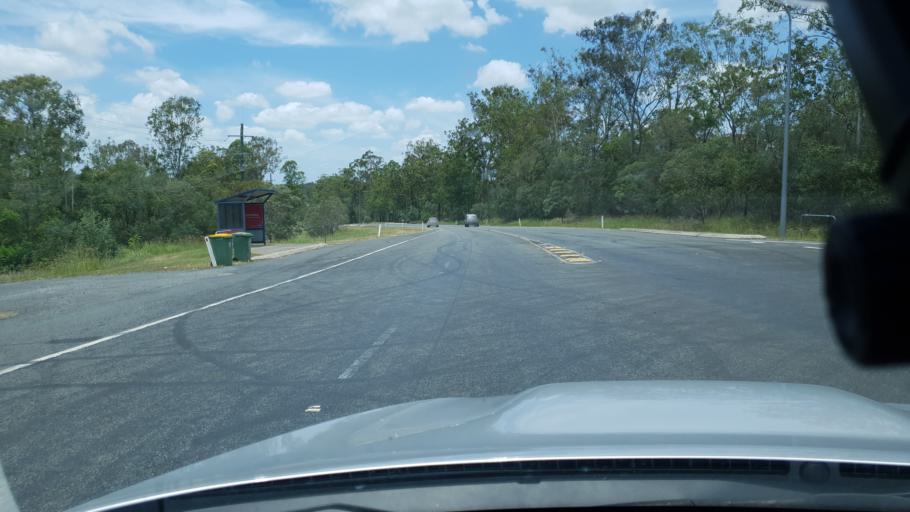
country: AU
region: Queensland
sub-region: Logan
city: North Maclean
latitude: -27.7741
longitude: 152.9808
